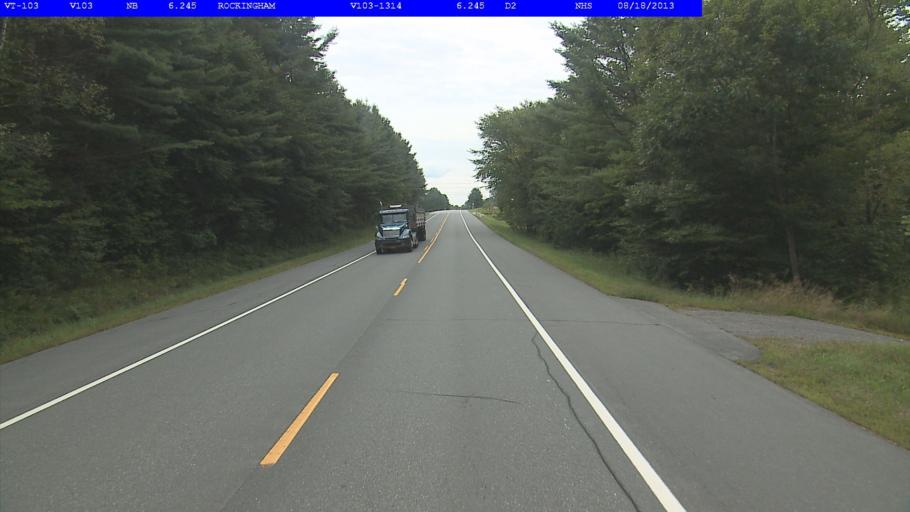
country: US
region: Vermont
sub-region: Windsor County
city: Chester
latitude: 43.2299
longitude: -72.5462
